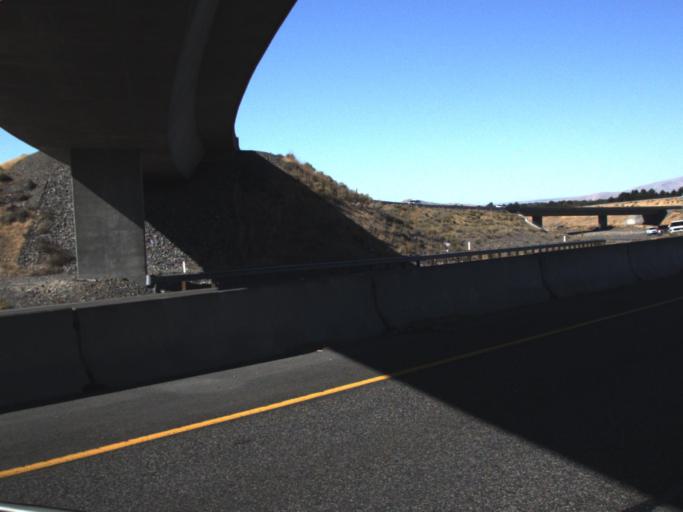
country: US
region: Washington
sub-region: Benton County
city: Richland
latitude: 46.2570
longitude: -119.2608
